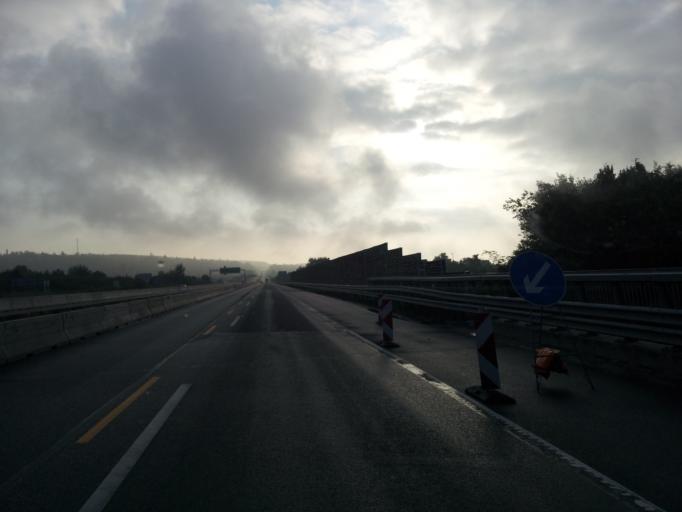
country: HU
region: Pest
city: Szada
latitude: 47.6144
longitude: 19.3333
